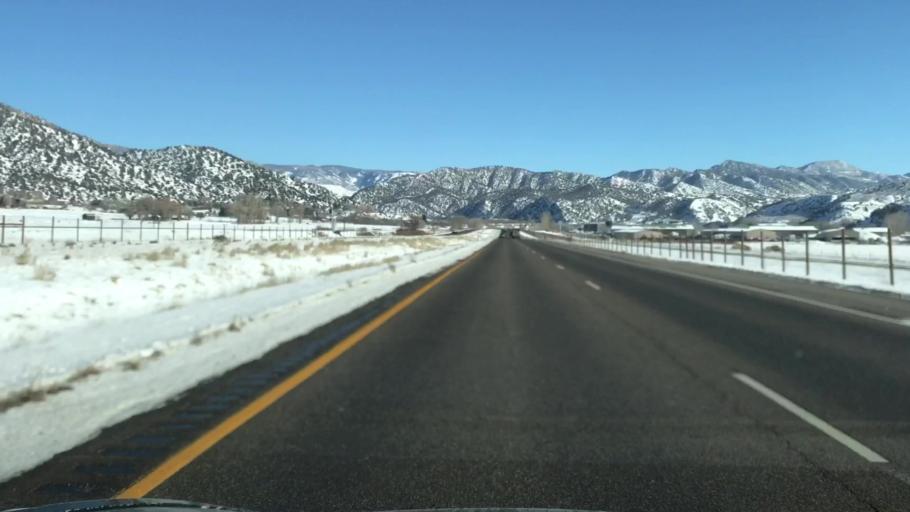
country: US
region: Colorado
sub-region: Garfield County
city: New Castle
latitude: 39.5541
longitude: -107.5783
